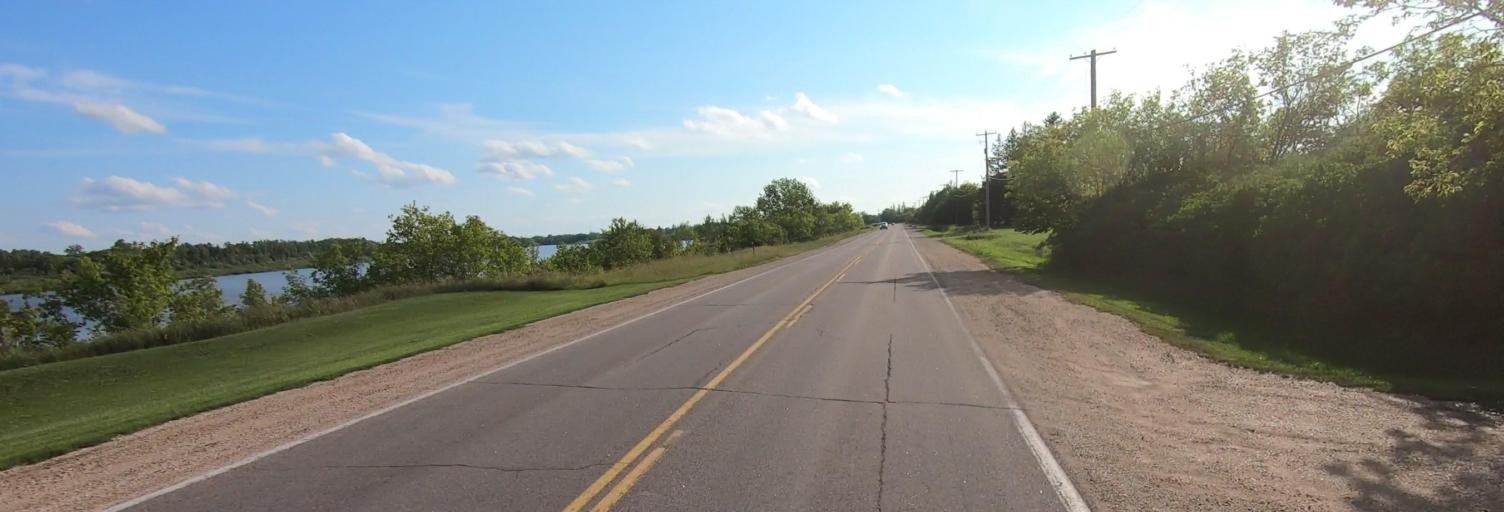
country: CA
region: Manitoba
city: Selkirk
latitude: 50.1793
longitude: -96.8509
